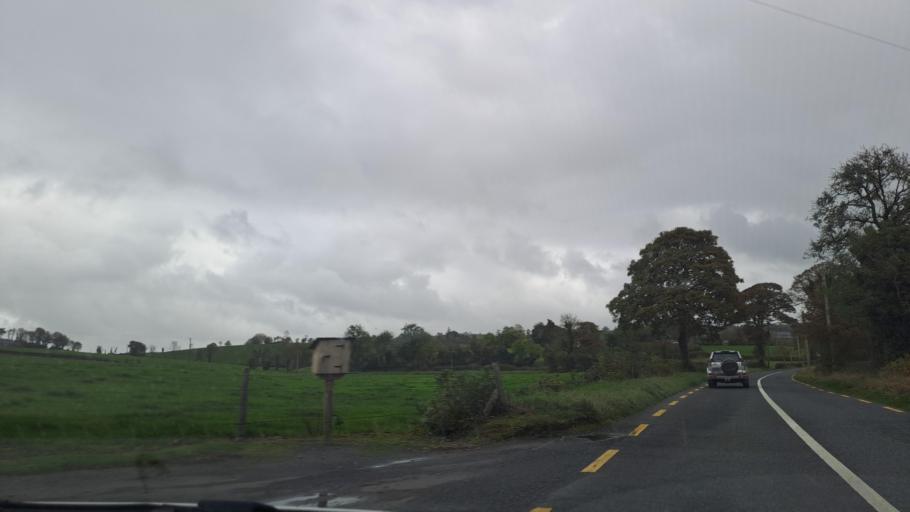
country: IE
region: Ulster
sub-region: An Cabhan
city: Bailieborough
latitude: 53.9371
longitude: -7.0168
